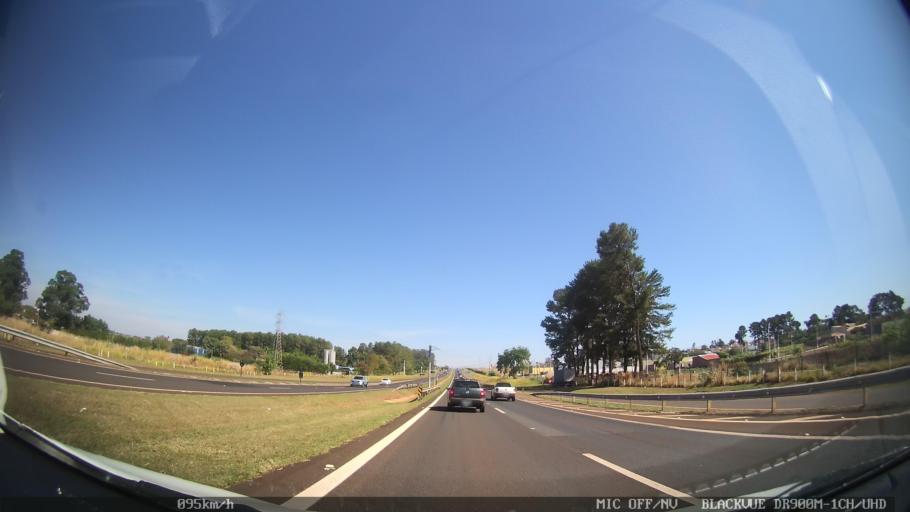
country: BR
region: Sao Paulo
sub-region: Ribeirao Preto
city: Ribeirao Preto
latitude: -21.1182
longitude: -47.8298
